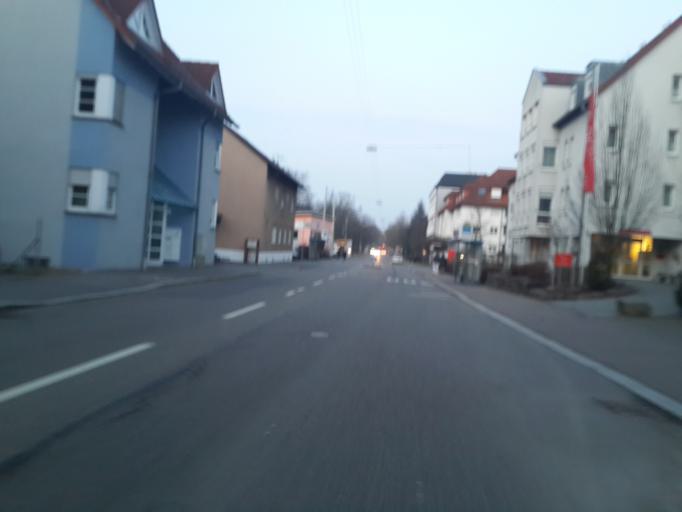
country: DE
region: Baden-Wuerttemberg
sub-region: Regierungsbezirk Stuttgart
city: Flein
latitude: 49.1205
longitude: 9.1915
